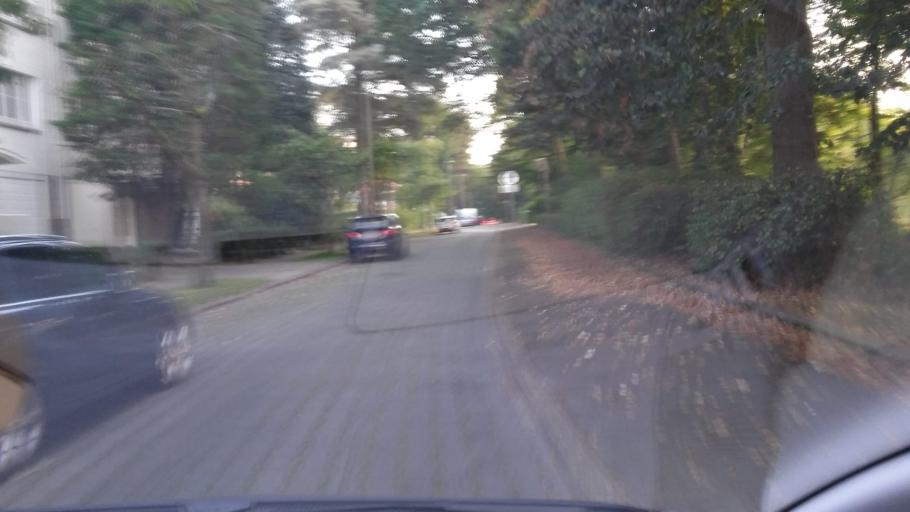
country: BE
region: Flanders
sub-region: Provincie Vlaams-Brabant
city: Hoeilaart
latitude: 50.8074
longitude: 4.4295
